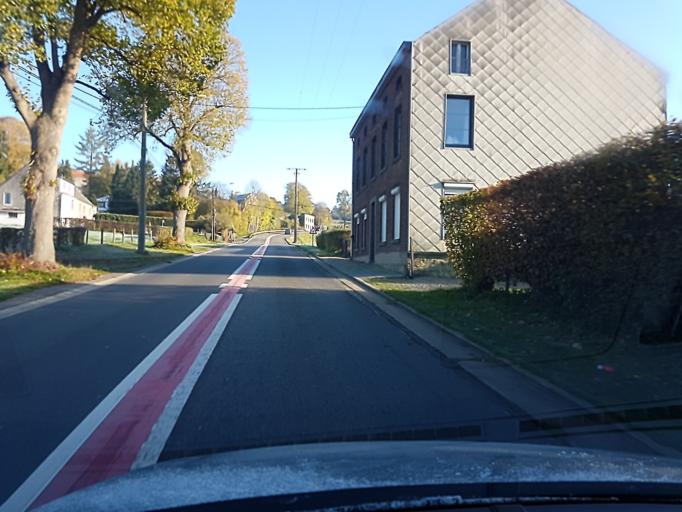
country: BE
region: Wallonia
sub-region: Province de Liege
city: Theux
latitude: 50.5443
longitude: 5.8314
